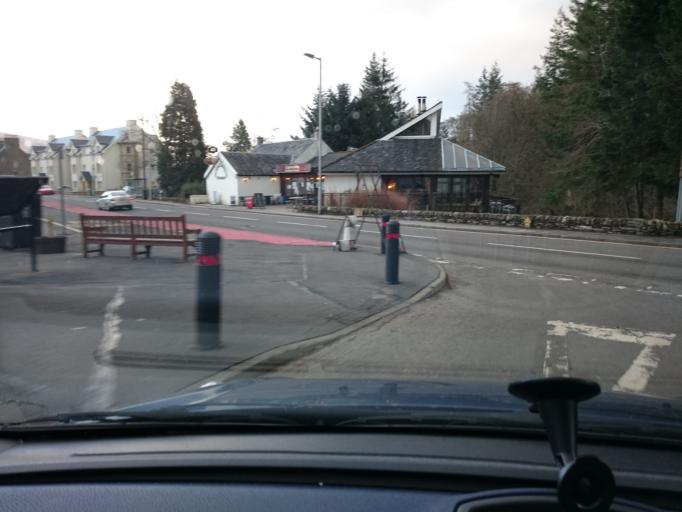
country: GB
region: Scotland
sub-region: Stirling
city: Callander
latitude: 56.4638
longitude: -4.3202
